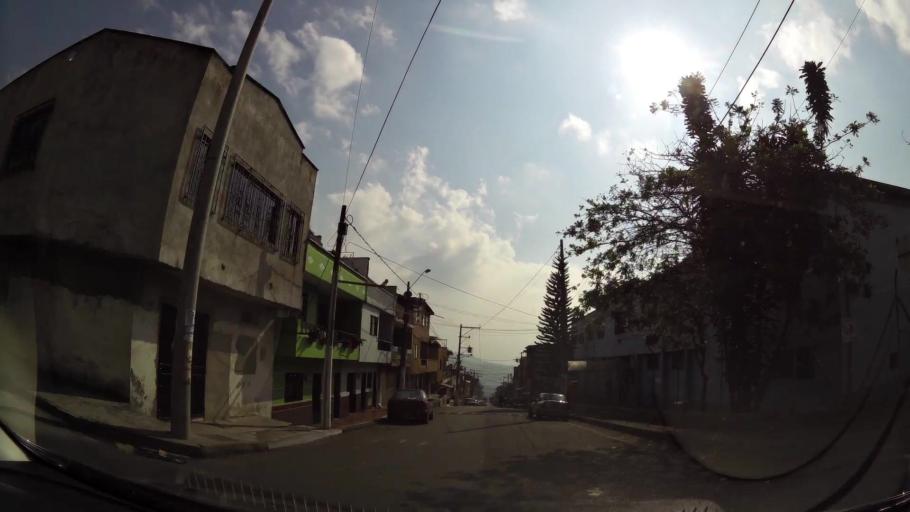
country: CO
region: Antioquia
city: La Estrella
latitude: 6.1707
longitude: -75.6420
